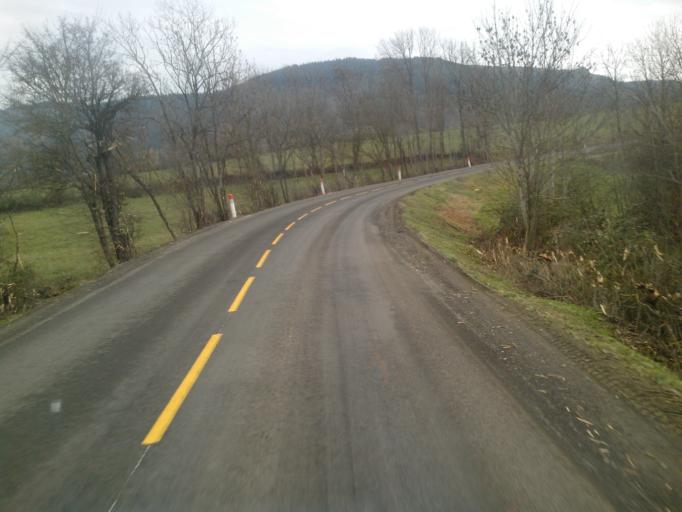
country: FR
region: Languedoc-Roussillon
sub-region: Departement de la Lozere
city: Mende
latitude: 44.4531
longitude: 3.5506
